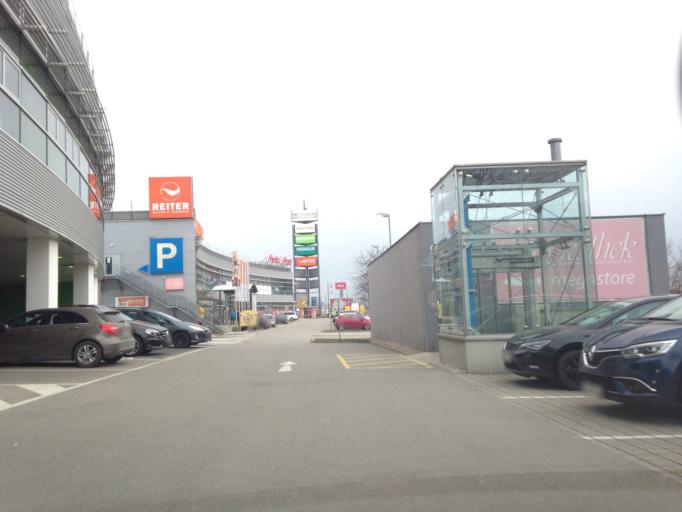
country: AT
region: Lower Austria
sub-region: Politischer Bezirk Wien-Umgebung
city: Gerasdorf bei Wien
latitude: 48.2498
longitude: 16.4676
